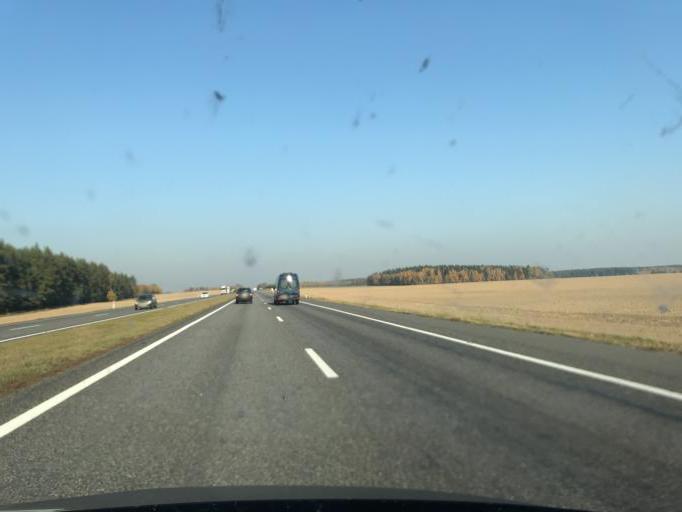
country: BY
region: Minsk
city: Haradzyeya
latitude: 53.3655
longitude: 26.4840
